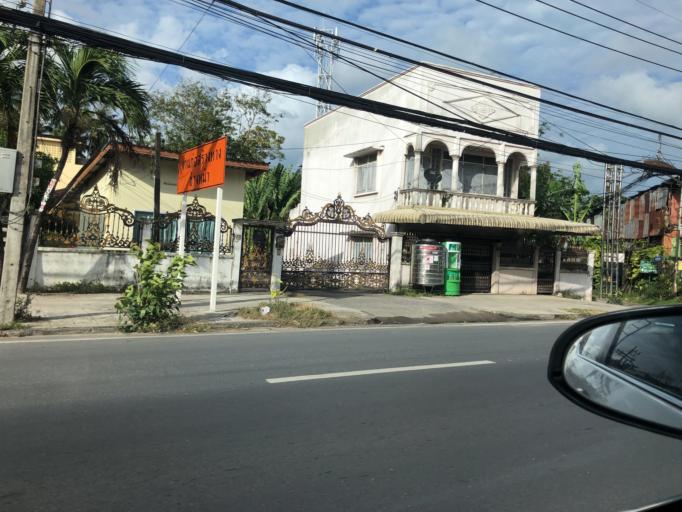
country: TH
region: Phuket
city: Ban Ko Kaeo
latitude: 7.9797
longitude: 98.3654
